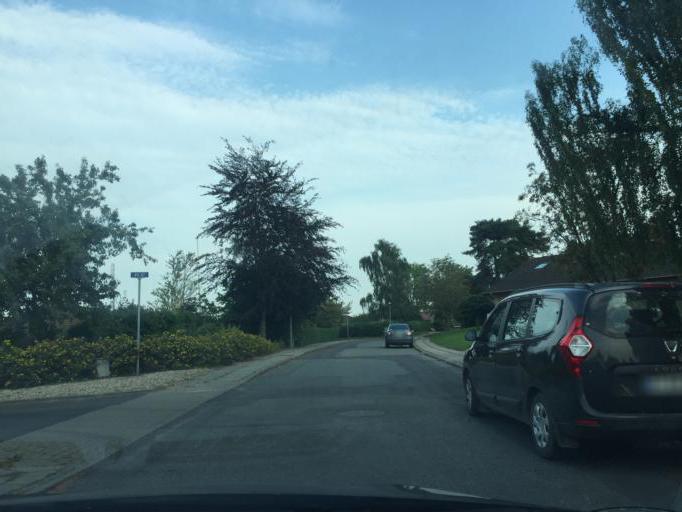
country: DK
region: South Denmark
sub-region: Kerteminde Kommune
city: Langeskov
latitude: 55.3106
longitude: 10.5896
